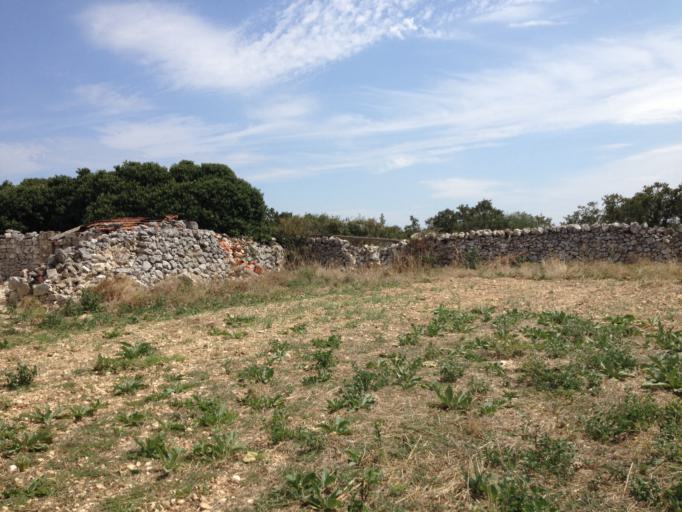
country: IT
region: Apulia
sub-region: Provincia di Bari
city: Sammichele di Bari
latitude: 40.8298
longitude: 16.9910
